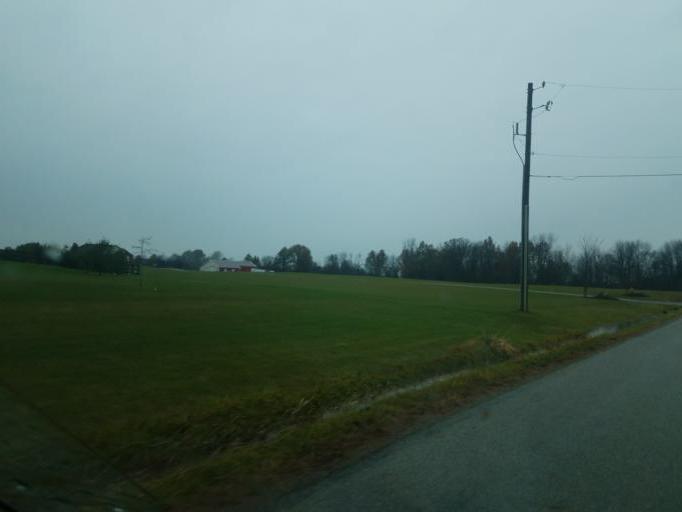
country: US
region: Ohio
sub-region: Knox County
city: Centerburg
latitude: 40.2865
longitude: -82.7244
